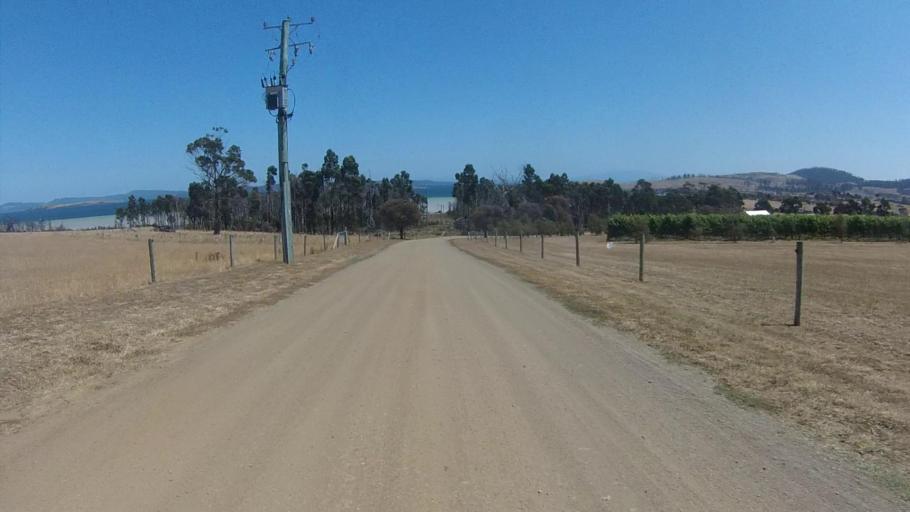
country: AU
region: Tasmania
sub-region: Sorell
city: Sorell
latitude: -42.8989
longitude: 147.8225
